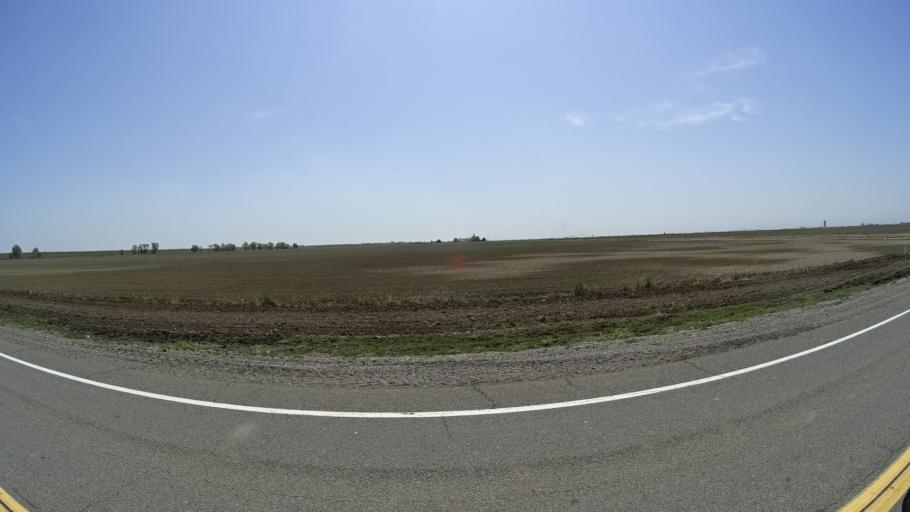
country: US
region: California
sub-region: Glenn County
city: Willows
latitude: 39.5217
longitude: -122.0358
